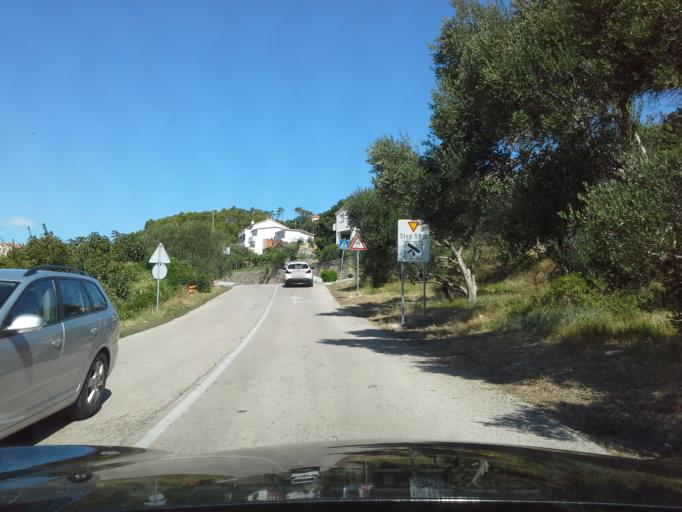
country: HR
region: Primorsko-Goranska
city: Banjol
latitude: 44.7590
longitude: 14.7688
